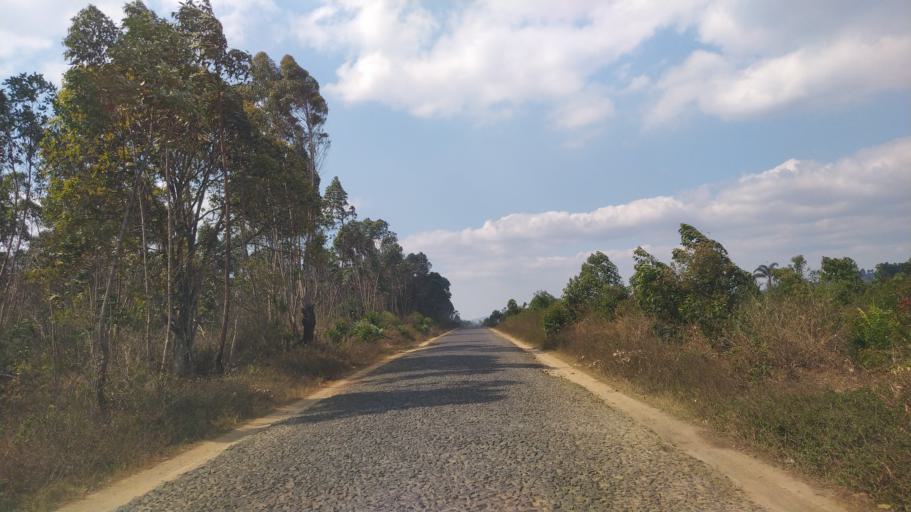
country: MG
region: Alaotra Mangoro
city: Moramanga
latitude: -18.7751
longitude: 48.2499
